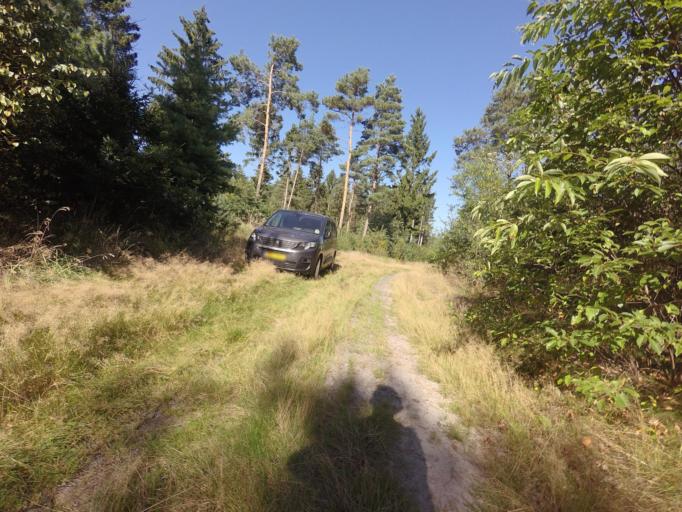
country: DE
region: Lower Saxony
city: Wielen
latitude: 52.5346
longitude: 6.7026
